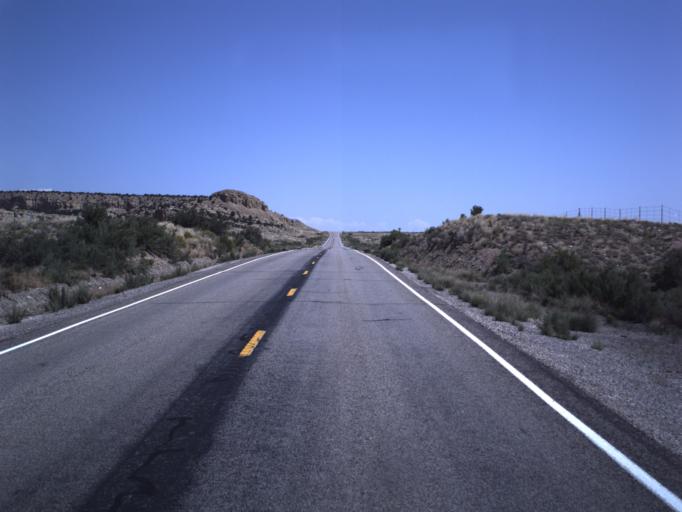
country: US
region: Utah
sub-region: Emery County
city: Ferron
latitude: 38.8167
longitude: -111.3308
